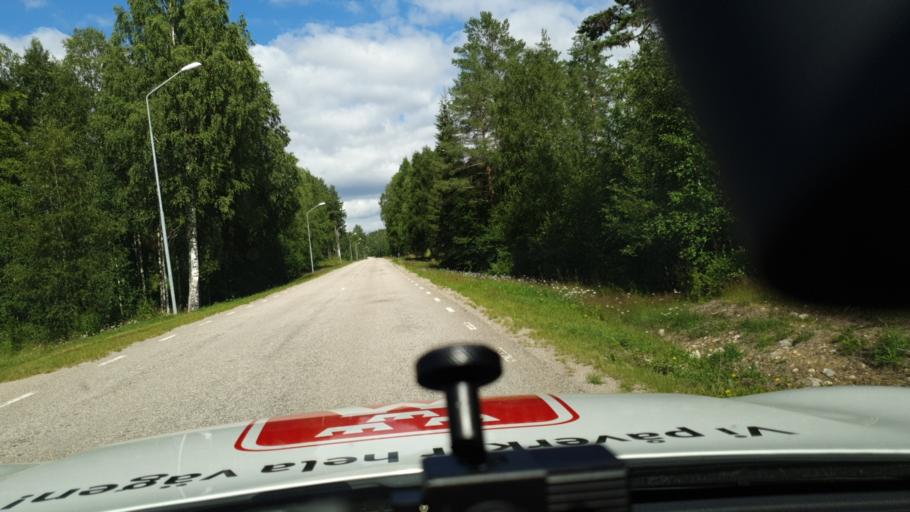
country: NO
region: Hedmark
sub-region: Trysil
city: Innbygda
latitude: 60.9615
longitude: 12.4754
